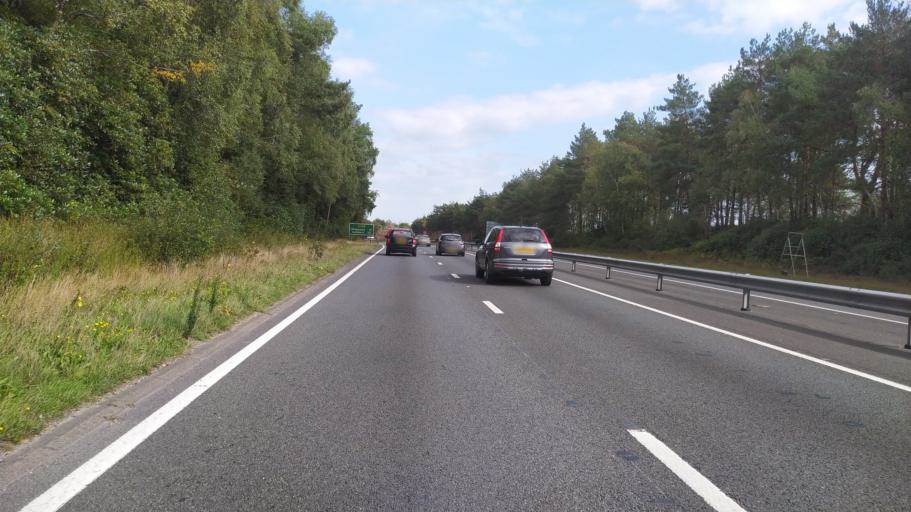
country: GB
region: England
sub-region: Dorset
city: Christchurch
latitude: 50.7678
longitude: -1.8082
